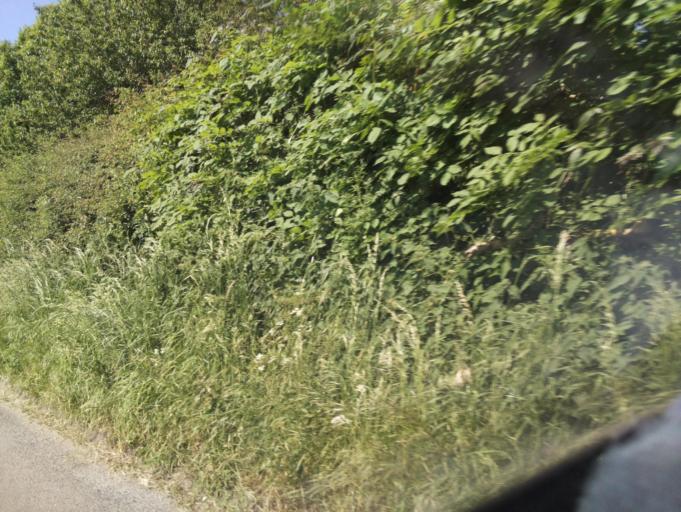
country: GB
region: England
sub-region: Hampshire
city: Abbotts Ann
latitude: 51.2419
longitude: -1.5693
